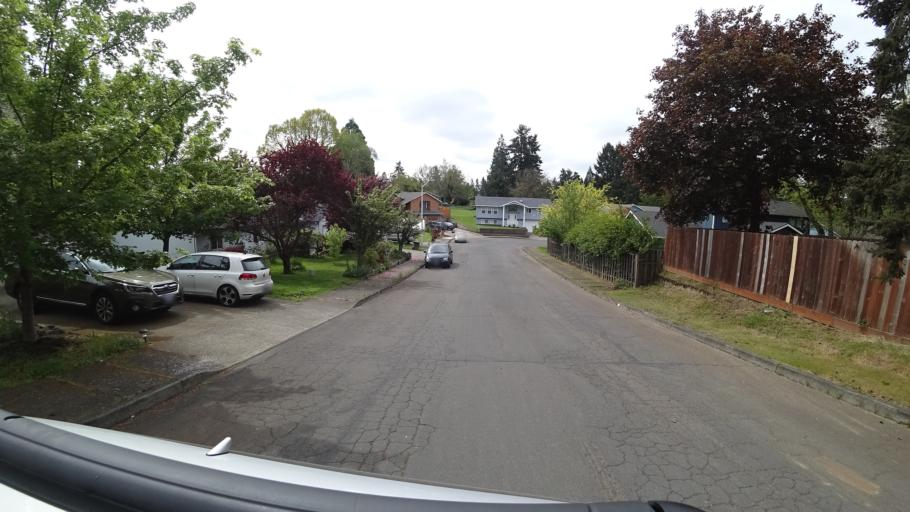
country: US
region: Oregon
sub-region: Washington County
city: Hillsboro
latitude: 45.5268
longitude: -122.9984
